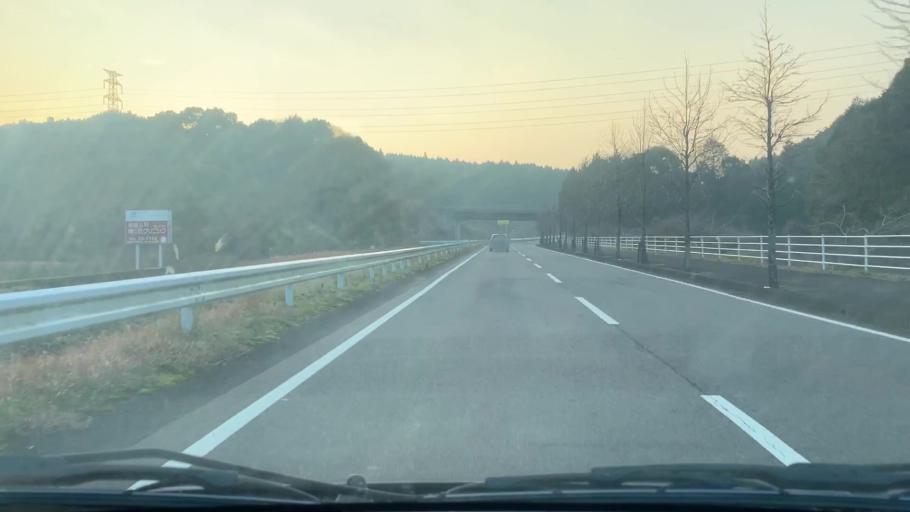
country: JP
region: Saga Prefecture
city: Imaricho-ko
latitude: 33.2596
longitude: 129.9268
